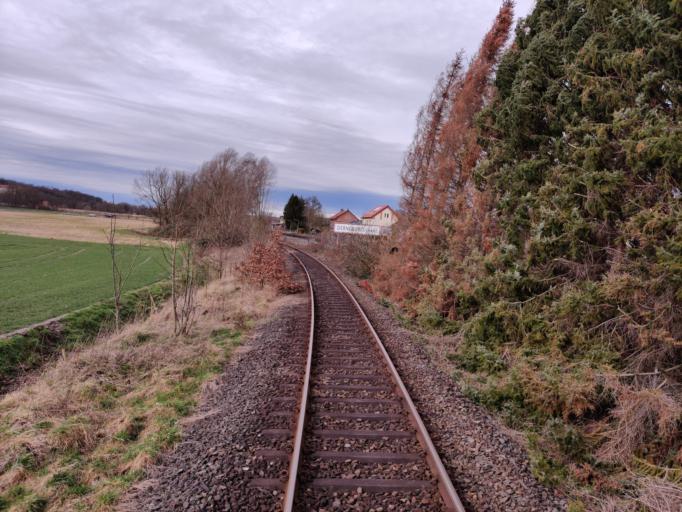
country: DE
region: Lower Saxony
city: Holle
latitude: 52.0956
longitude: 10.1483
